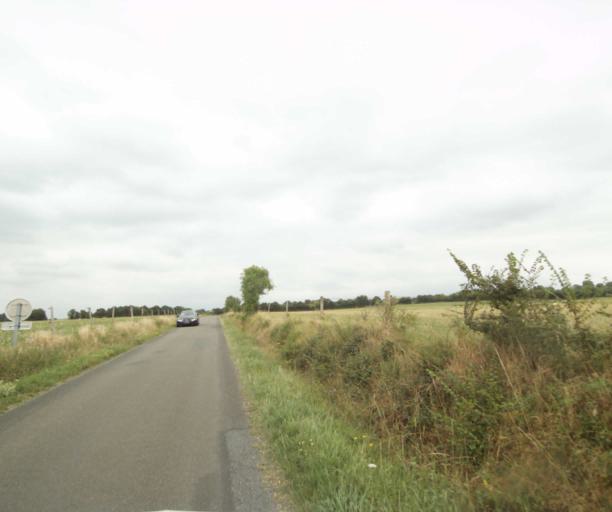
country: FR
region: Pays de la Loire
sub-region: Departement de la Sarthe
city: Solesmes
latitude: 47.8503
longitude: -0.2868
